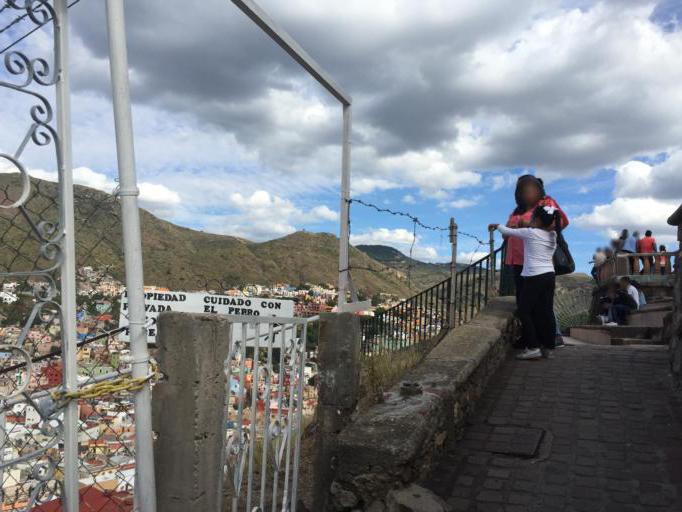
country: MX
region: Guanajuato
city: Guanajuato
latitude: 21.0147
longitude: -101.2546
